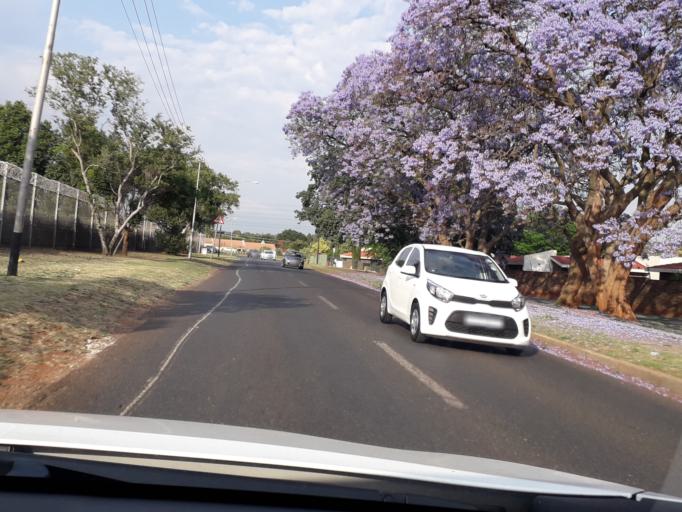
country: ZA
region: Gauteng
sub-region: City of Johannesburg Metropolitan Municipality
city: Johannesburg
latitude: -26.1626
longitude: 27.9829
